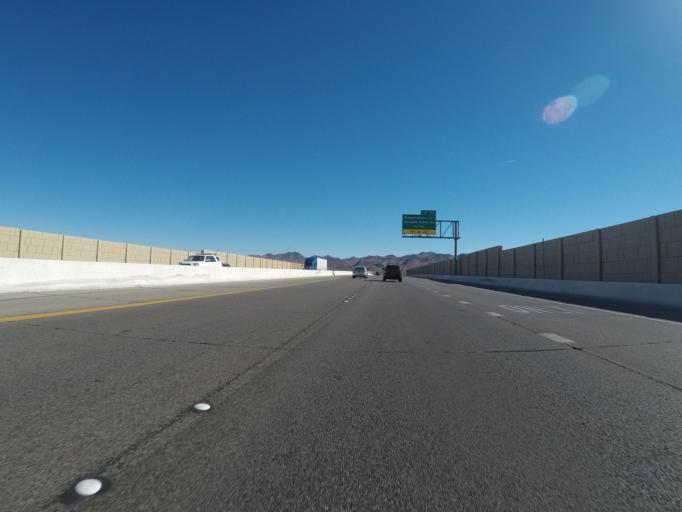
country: US
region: Nevada
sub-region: Clark County
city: Henderson
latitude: 35.9999
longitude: -114.9524
